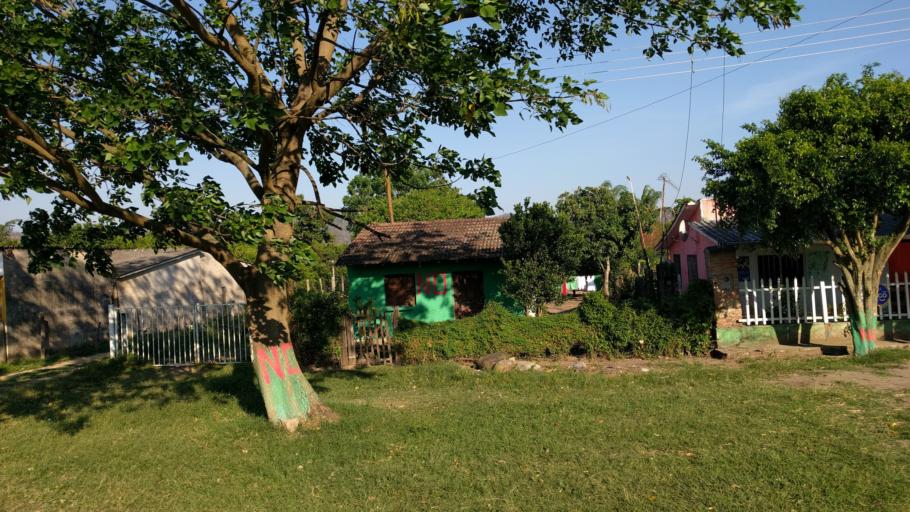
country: BO
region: Santa Cruz
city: Jorochito
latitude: -18.1255
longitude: -63.4655
